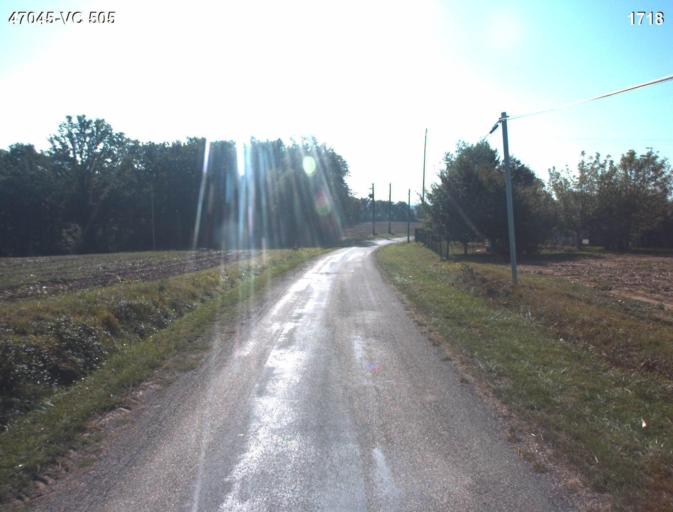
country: FR
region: Aquitaine
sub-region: Departement du Lot-et-Garonne
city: Nerac
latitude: 44.1491
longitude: 0.4155
